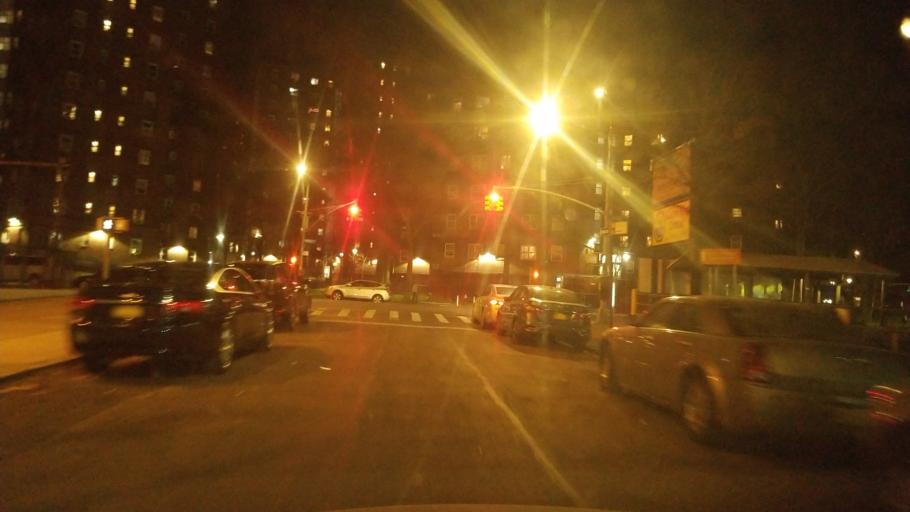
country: US
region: New York
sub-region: New York County
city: Manhattan
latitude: 40.8132
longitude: -73.9263
